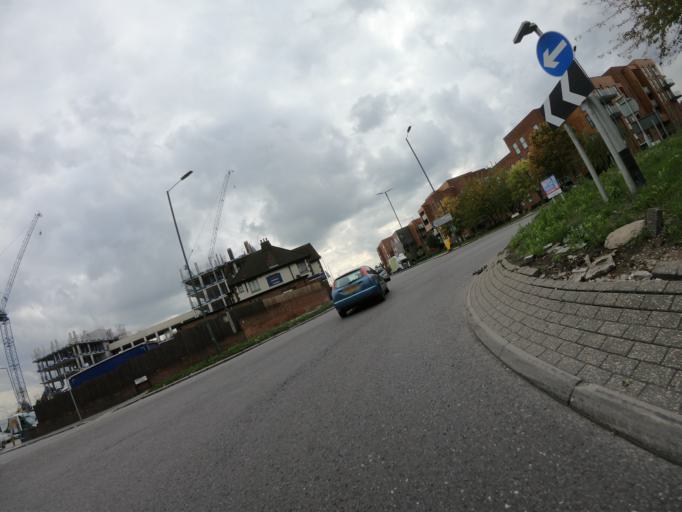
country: GB
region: England
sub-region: Greater London
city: Erith
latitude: 51.4737
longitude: 0.1814
